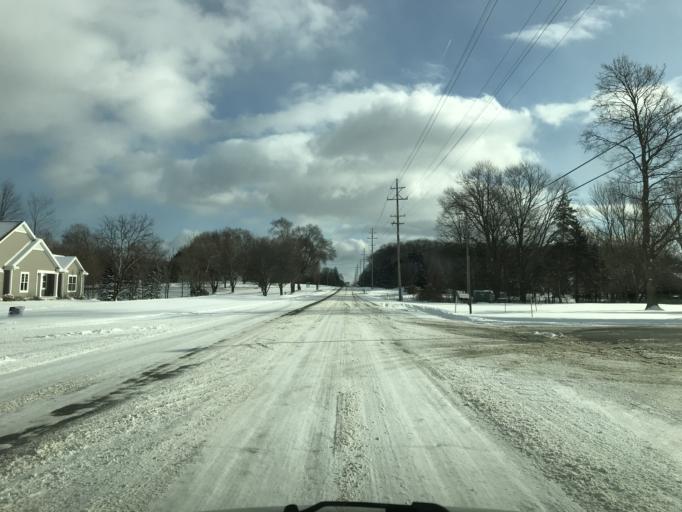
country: US
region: Michigan
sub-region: Kent County
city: Byron Center
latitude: 42.8268
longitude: -85.7167
